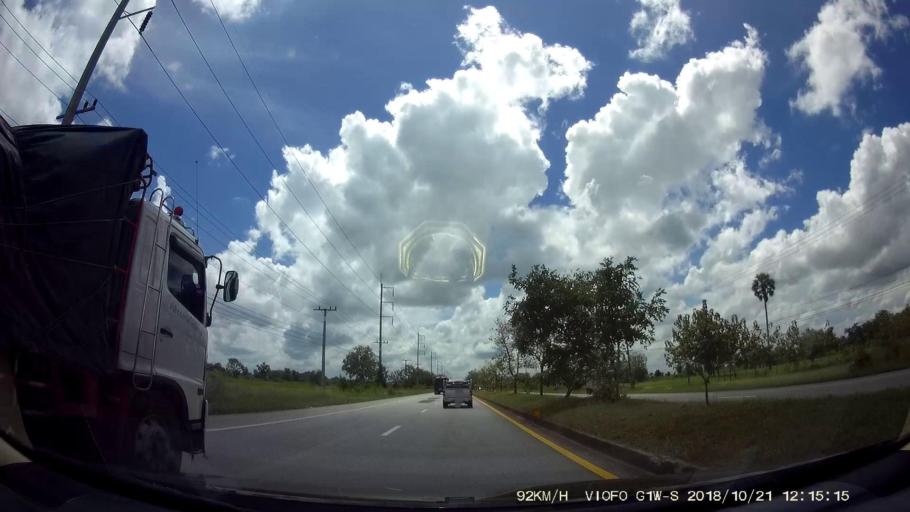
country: TH
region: Nakhon Ratchasima
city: Dan Khun Thot
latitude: 15.3659
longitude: 101.8315
